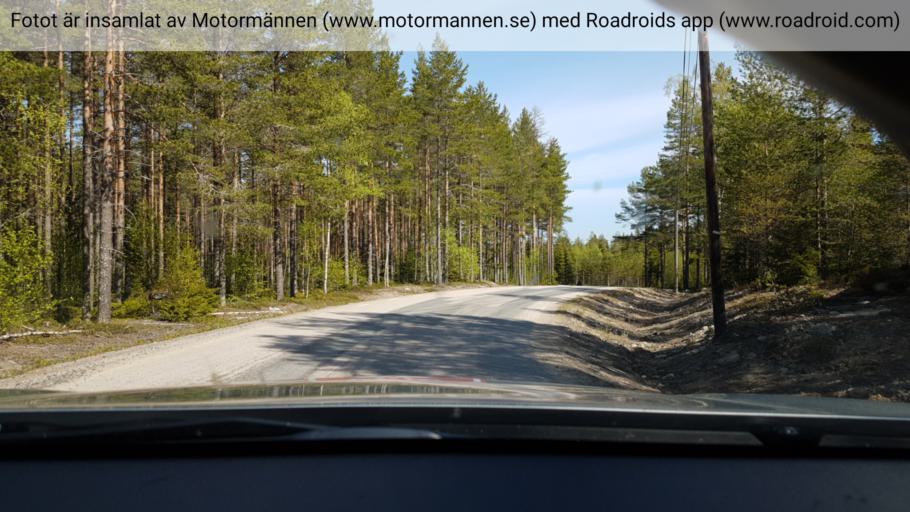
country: SE
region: Vaesterbotten
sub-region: Umea Kommun
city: Saevar
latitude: 63.8220
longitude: 20.5872
